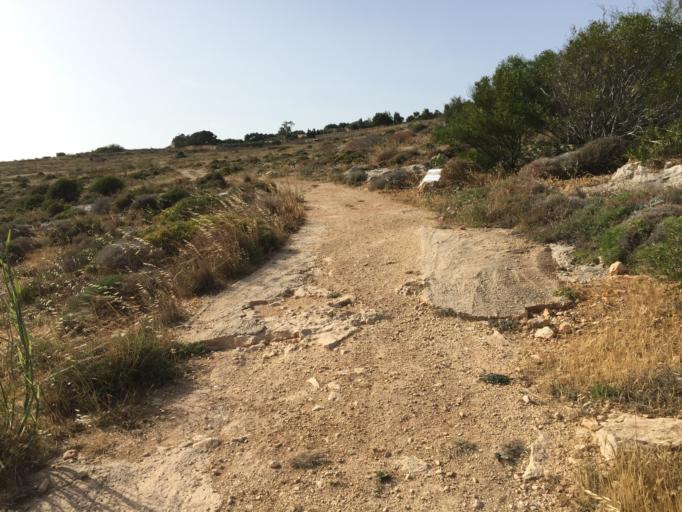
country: MT
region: Il-Qrendi
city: Qrendi
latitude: 35.8272
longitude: 14.4383
